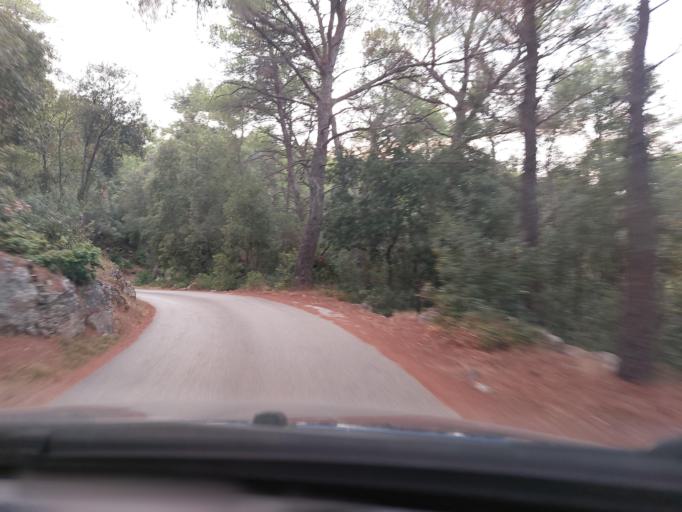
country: HR
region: Dubrovacko-Neretvanska
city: Smokvica
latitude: 42.7618
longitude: 16.9105
